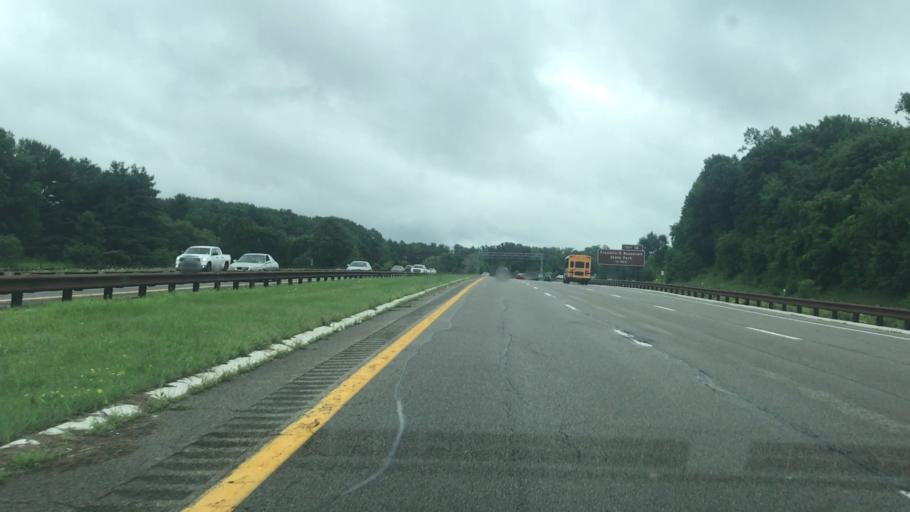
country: US
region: New York
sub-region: Westchester County
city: Jefferson Valley-Yorktown
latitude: 41.2910
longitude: -73.8208
